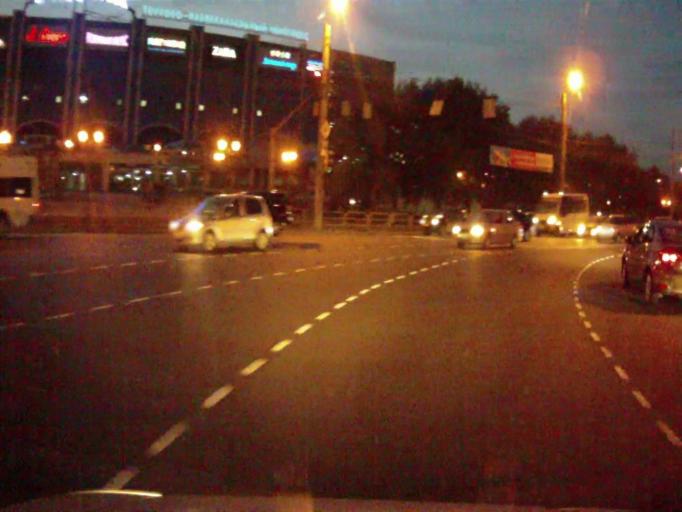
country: RU
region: Chelyabinsk
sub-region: Gorod Chelyabinsk
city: Chelyabinsk
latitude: 55.1708
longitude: 61.3585
